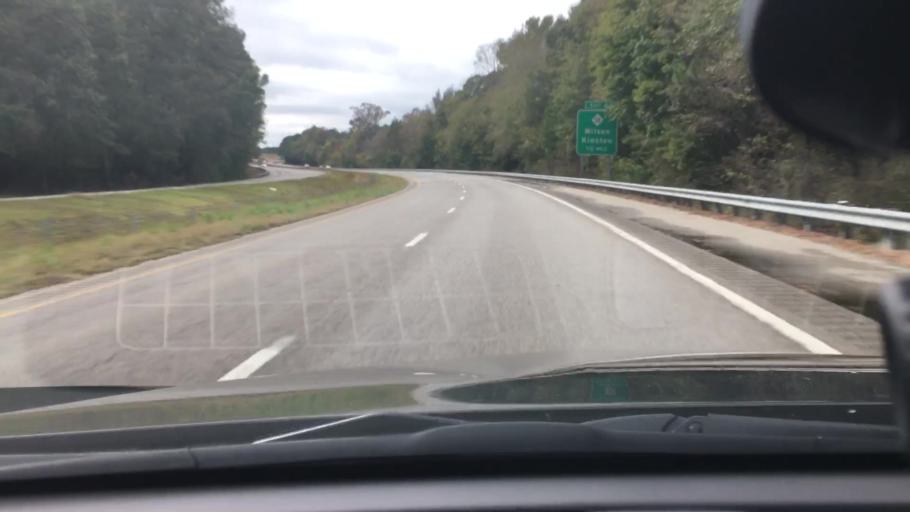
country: US
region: North Carolina
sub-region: Wilson County
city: Wilson
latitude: 35.6801
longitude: -77.8441
